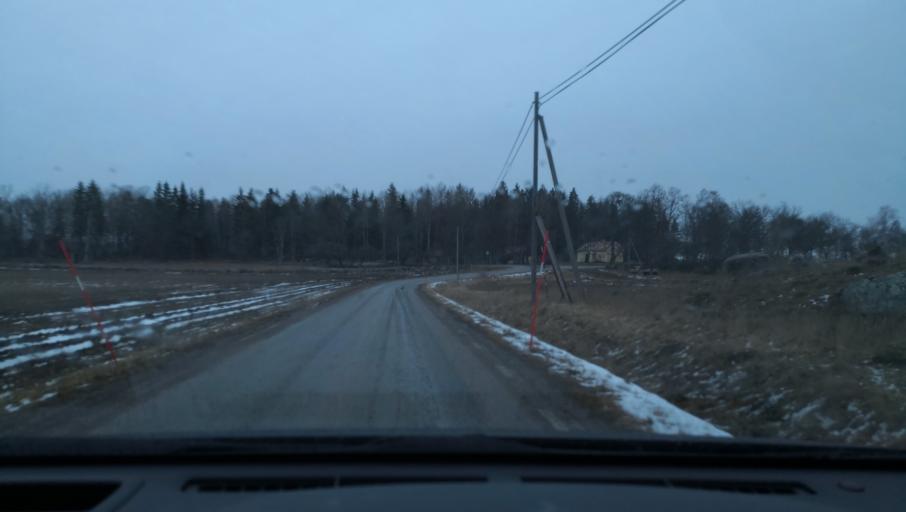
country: SE
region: Uppsala
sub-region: Enkopings Kommun
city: Hummelsta
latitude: 59.4650
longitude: 16.8405
